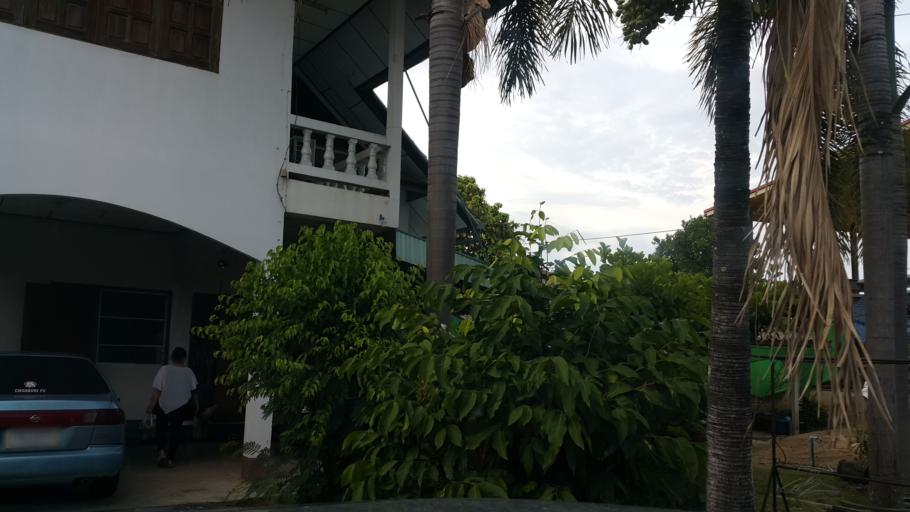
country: TH
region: Chiang Rai
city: Chiang Rai
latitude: 19.9273
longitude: 99.8497
